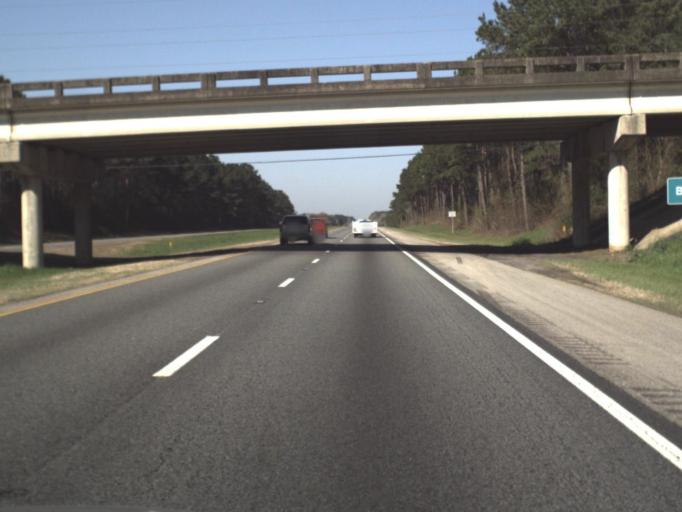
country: US
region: Florida
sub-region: Leon County
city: Tallahassee
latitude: 30.4783
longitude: -84.0913
